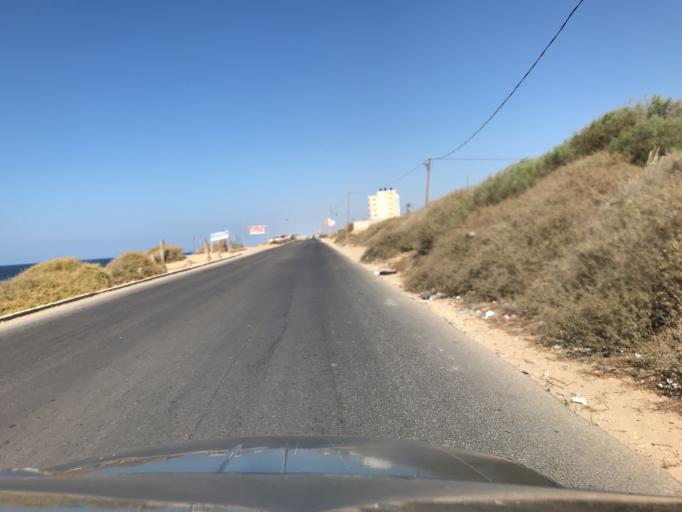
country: PS
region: Gaza Strip
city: Az Zuwaydah
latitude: 31.4449
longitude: 34.3576
